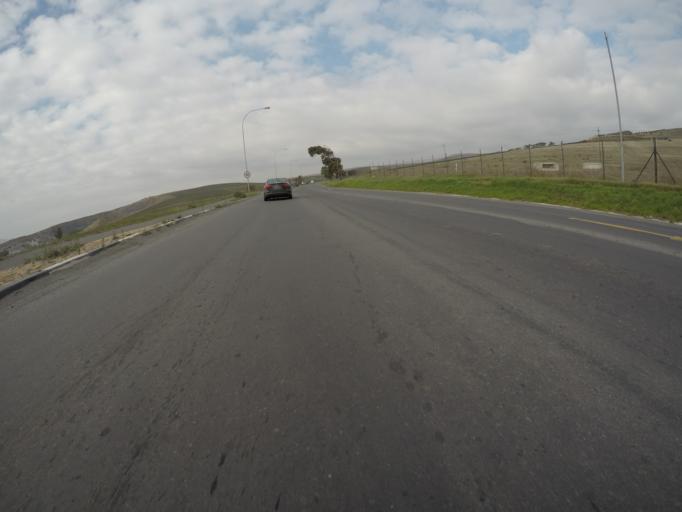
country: ZA
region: Western Cape
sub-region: City of Cape Town
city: Sunset Beach
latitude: -33.8223
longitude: 18.5583
